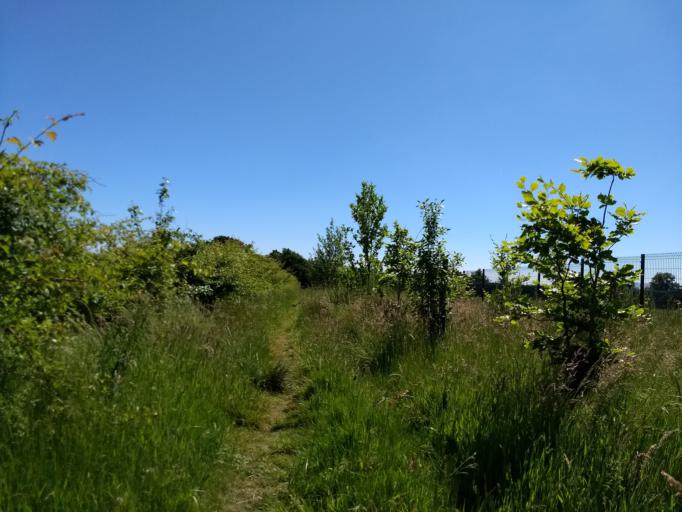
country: GB
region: England
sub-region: Isle of Wight
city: Seaview
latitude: 50.7008
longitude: -1.1212
